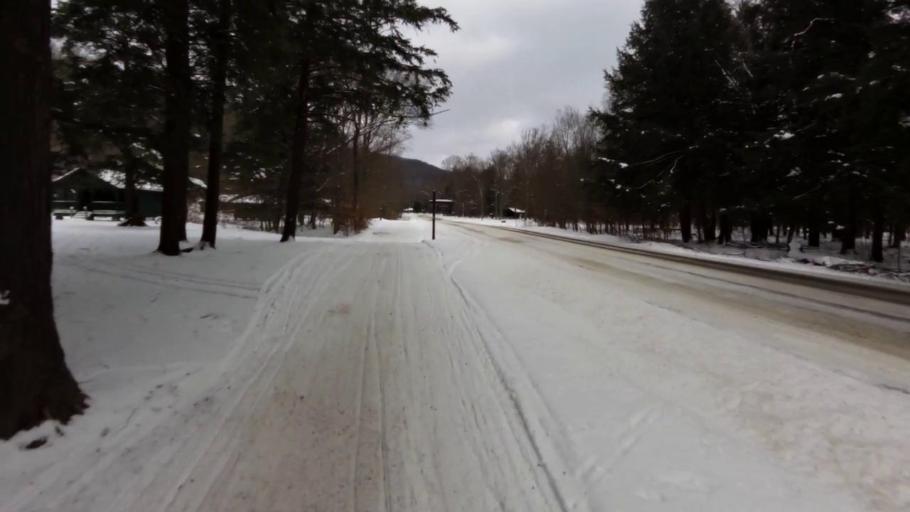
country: US
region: New York
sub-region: Cattaraugus County
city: Salamanca
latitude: 42.0111
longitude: -78.8170
